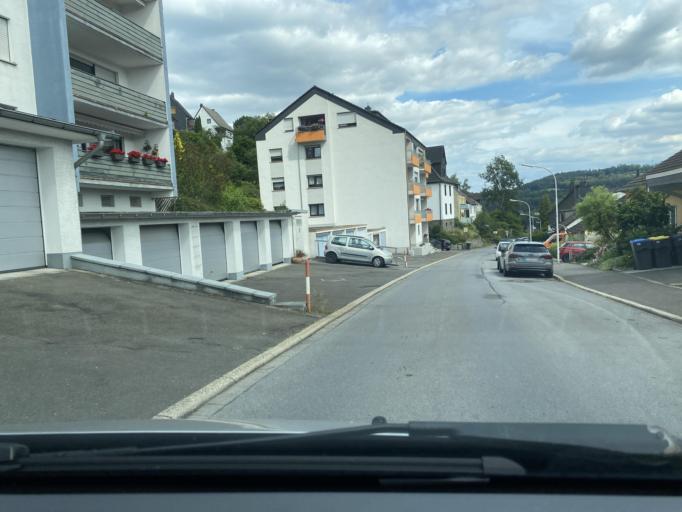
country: DE
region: North Rhine-Westphalia
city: Werdohl
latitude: 51.2642
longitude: 7.7666
